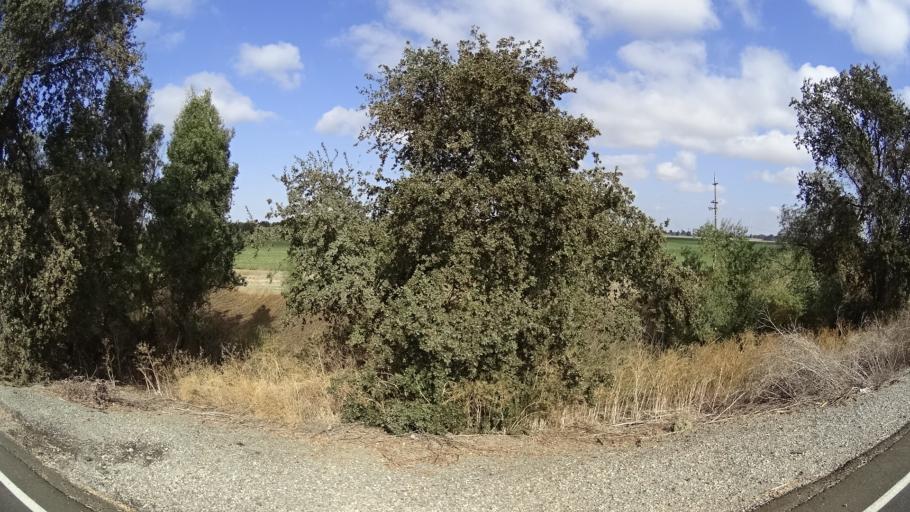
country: US
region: California
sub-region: Yolo County
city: Woodland
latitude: 38.7486
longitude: -121.6910
